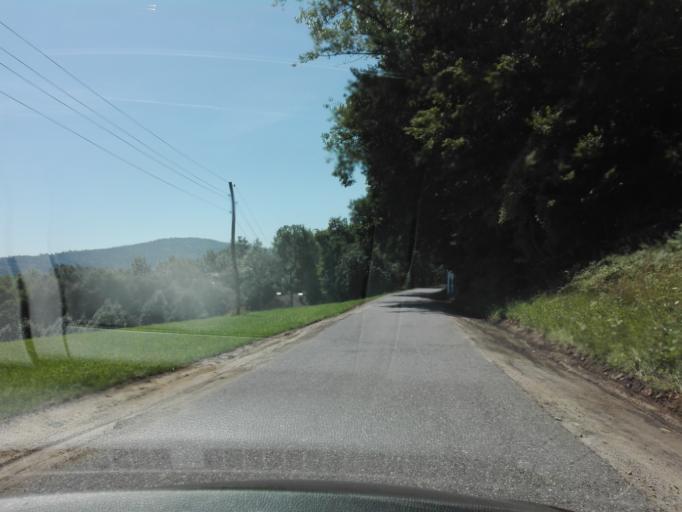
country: AT
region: Upper Austria
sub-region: Politischer Bezirk Urfahr-Umgebung
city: Gallneukirchen
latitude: 48.3266
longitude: 14.3972
